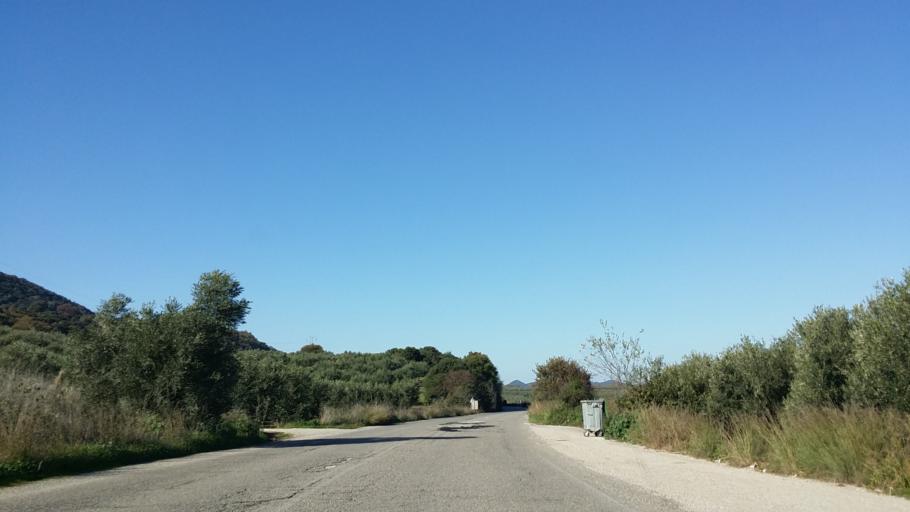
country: GR
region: West Greece
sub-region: Nomos Aitolias kai Akarnanias
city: Monastirakion
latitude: 38.8701
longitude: 21.0500
